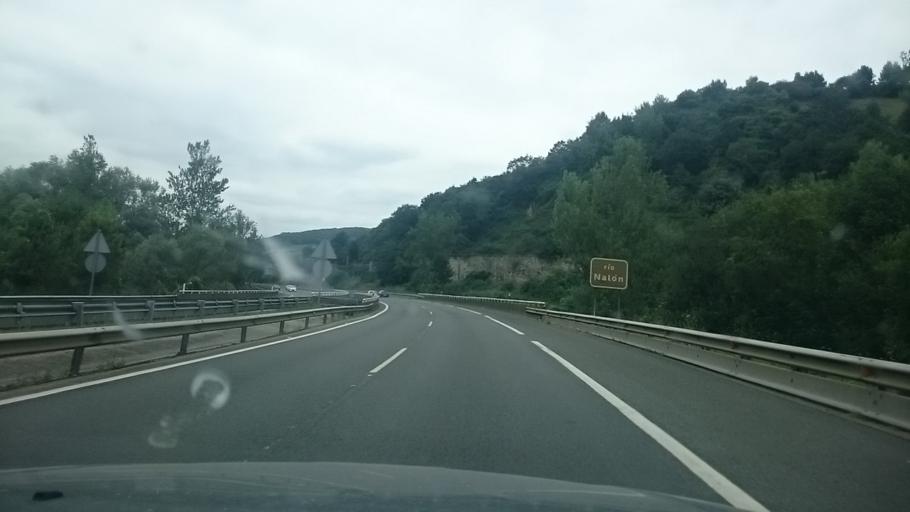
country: ES
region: Asturias
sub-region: Province of Asturias
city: Castandiello
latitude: 43.3025
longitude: -5.8508
